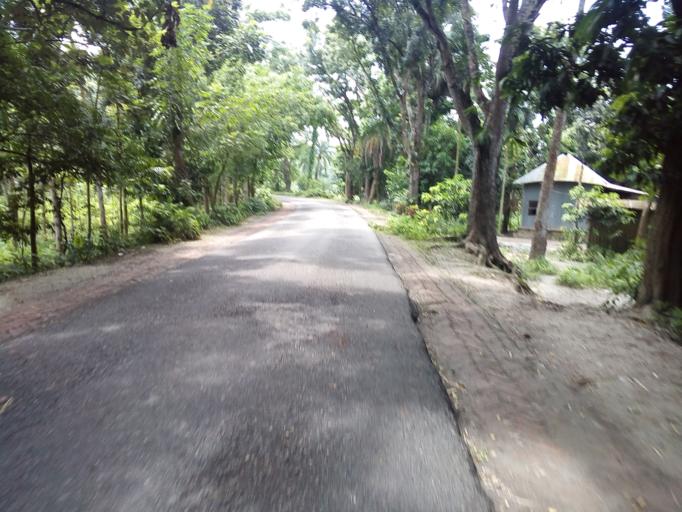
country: BD
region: Dhaka
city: Faridpur
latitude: 23.5698
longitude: 89.6282
